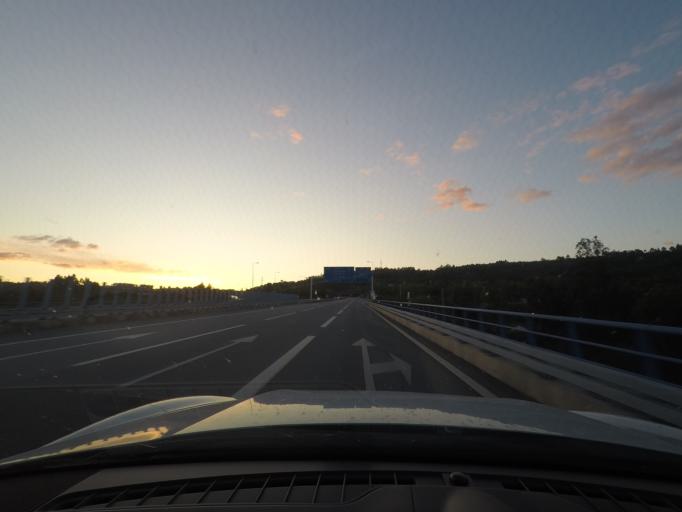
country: PT
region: Braga
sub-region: Vizela
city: Vizela
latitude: 41.4012
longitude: -8.2503
